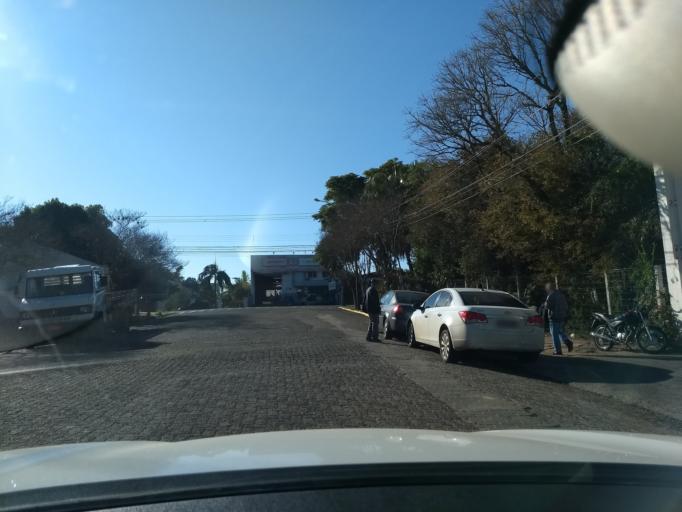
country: BR
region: Rio Grande do Sul
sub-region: Santa Cruz Do Sul
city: Santa Cruz do Sul
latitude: -29.7195
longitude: -52.4421
